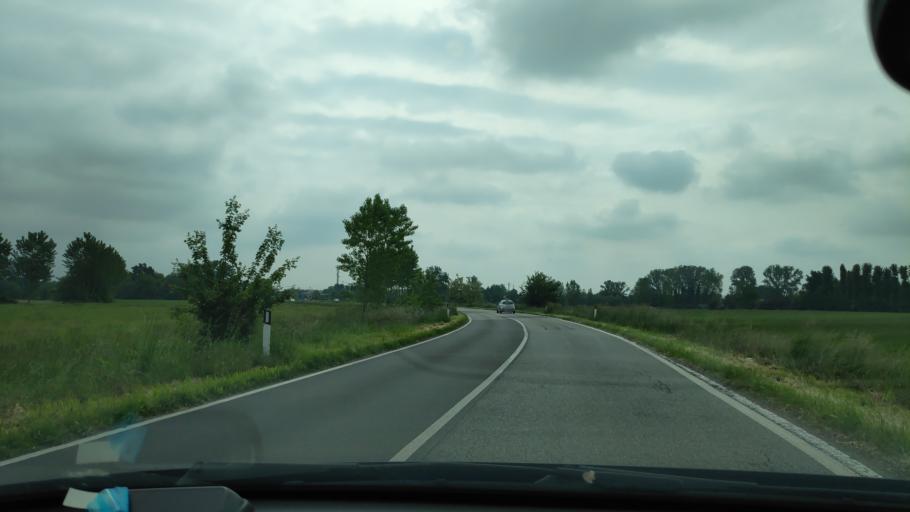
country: IT
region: Lombardy
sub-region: Citta metropolitana di Milano
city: Tribiano
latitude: 45.4214
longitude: 9.3791
